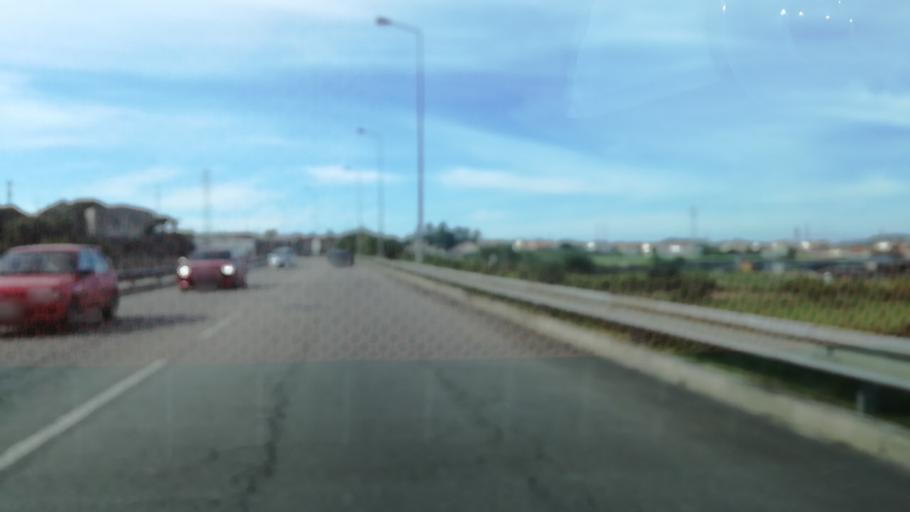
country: PT
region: Porto
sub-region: Valongo
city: Ermesinde
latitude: 41.2253
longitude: -8.5649
